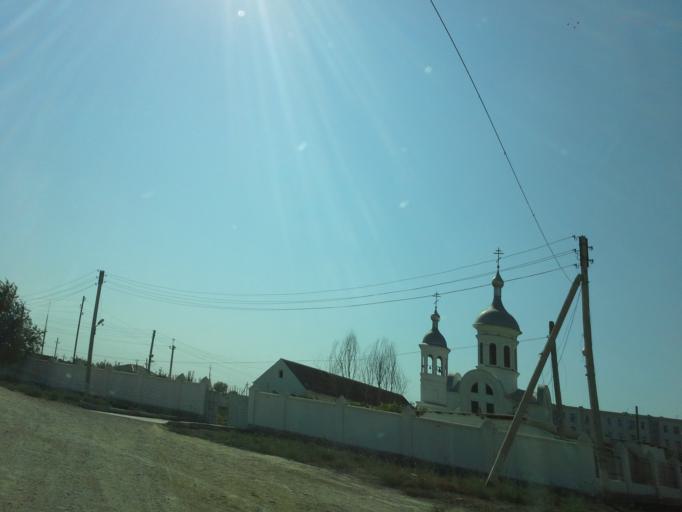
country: TM
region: Dasoguz
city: Dasoguz
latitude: 41.8226
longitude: 59.9668
